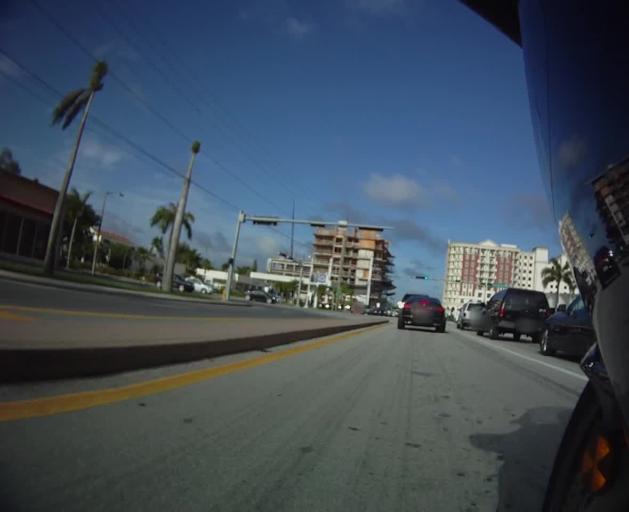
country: US
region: Florida
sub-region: Miami-Dade County
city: Coral Gables
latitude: 25.7349
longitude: -80.2591
